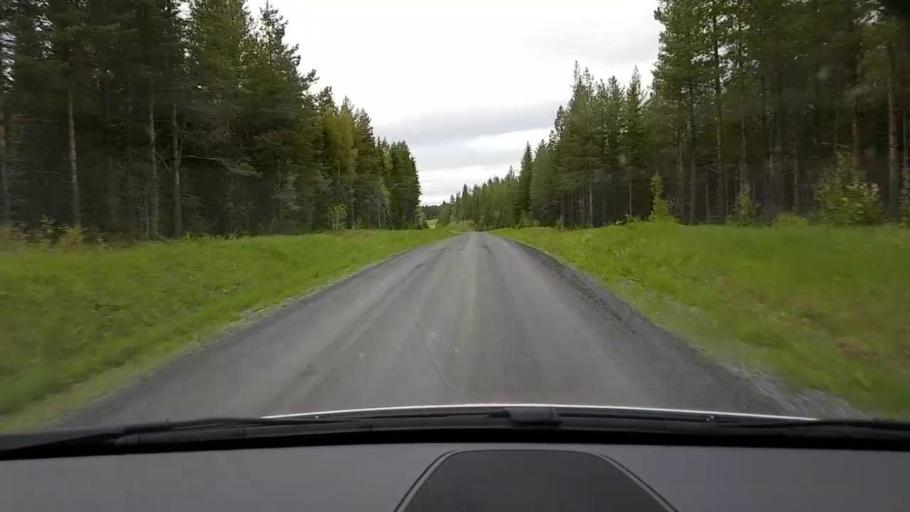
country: SE
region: Jaemtland
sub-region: Krokoms Kommun
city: Krokom
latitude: 63.3033
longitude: 14.3969
